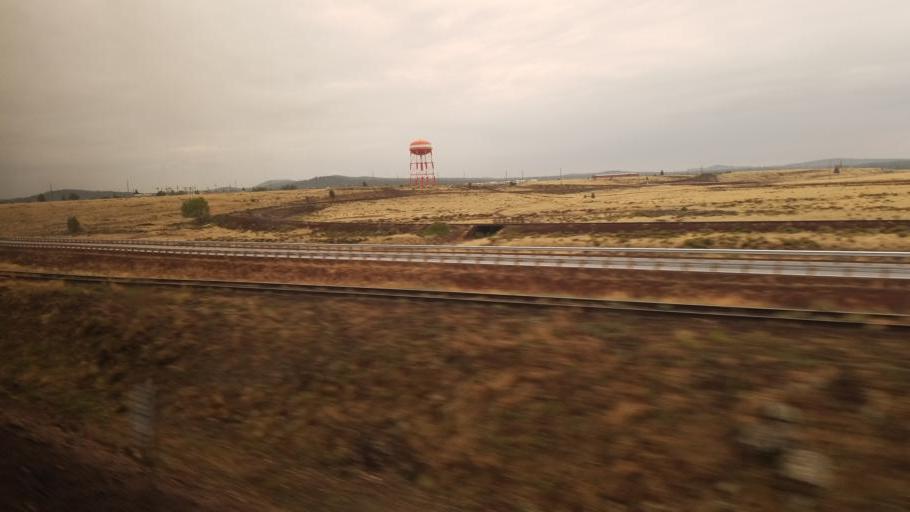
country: US
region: Arizona
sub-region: Coconino County
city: Parks
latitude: 35.2346
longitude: -111.8300
